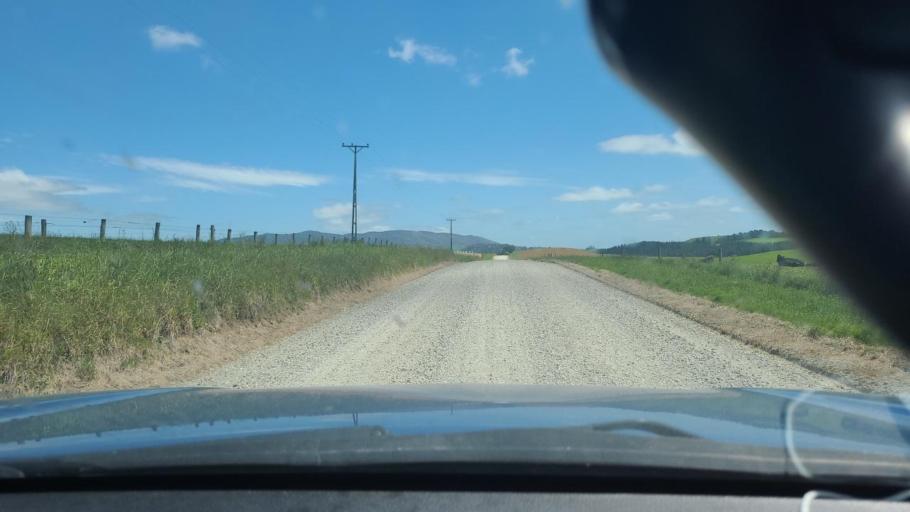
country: NZ
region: Southland
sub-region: Gore District
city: Gore
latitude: -46.4178
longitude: 169.0868
